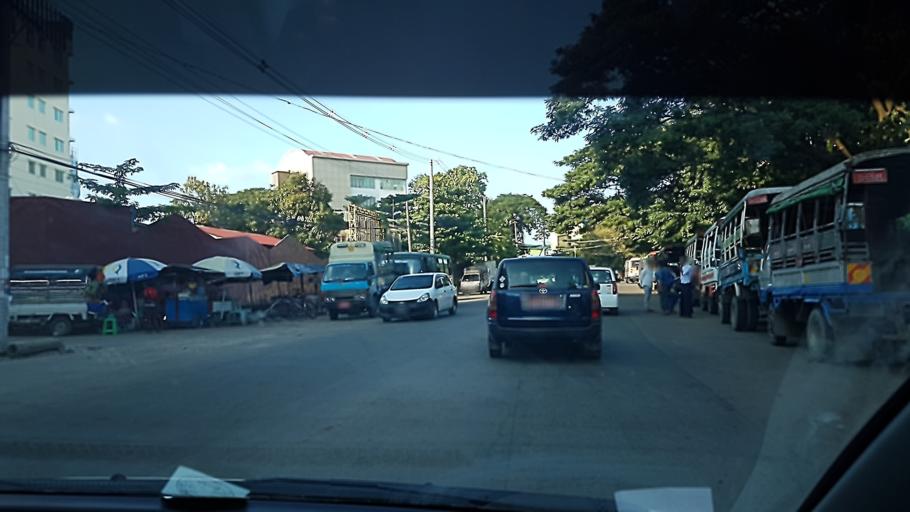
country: MM
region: Yangon
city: Yangon
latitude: 16.8285
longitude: 96.1881
